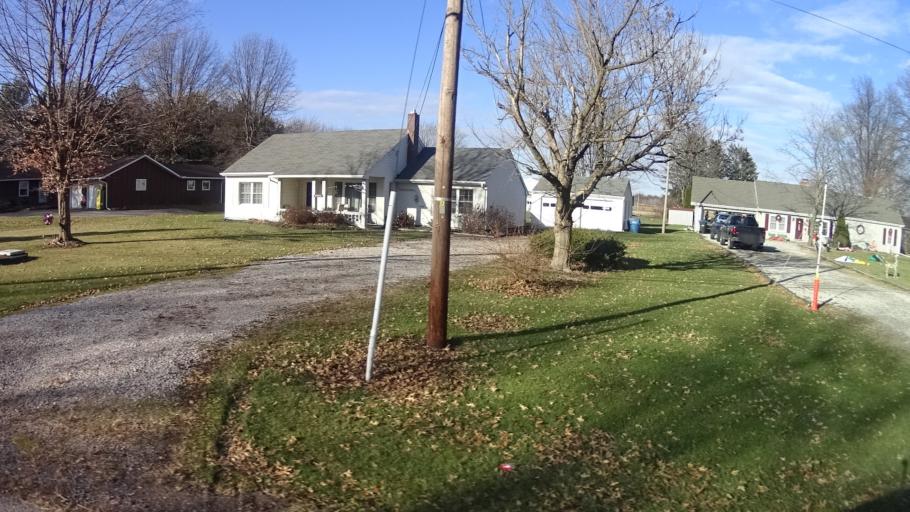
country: US
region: Ohio
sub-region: Lorain County
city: North Ridgeville
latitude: 41.3713
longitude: -82.0422
